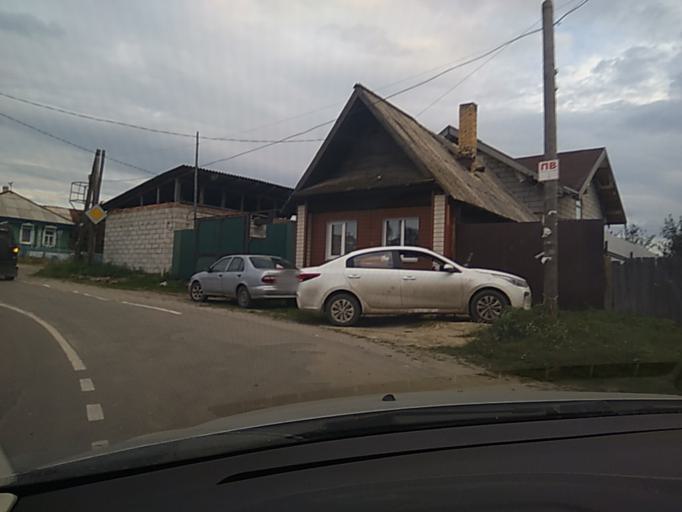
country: RU
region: Chelyabinsk
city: Kyshtym
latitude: 55.6940
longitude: 60.5306
